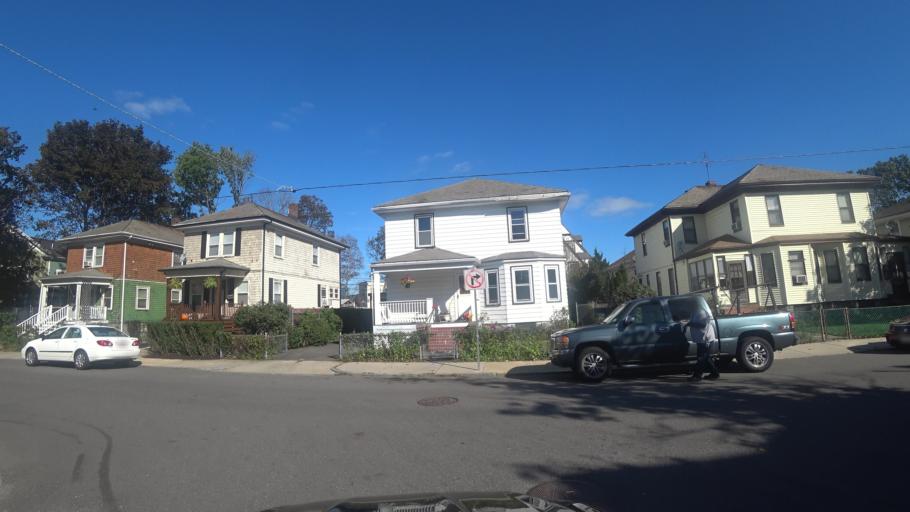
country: US
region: Massachusetts
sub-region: Suffolk County
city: South Boston
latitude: 42.3203
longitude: -71.0643
